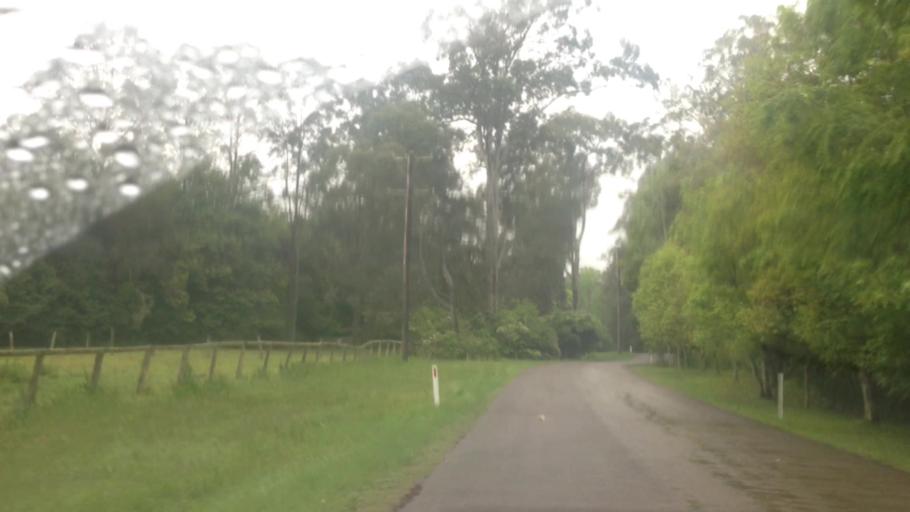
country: AU
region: New South Wales
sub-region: Wyong Shire
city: Little Jilliby
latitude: -33.1900
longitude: 151.3604
